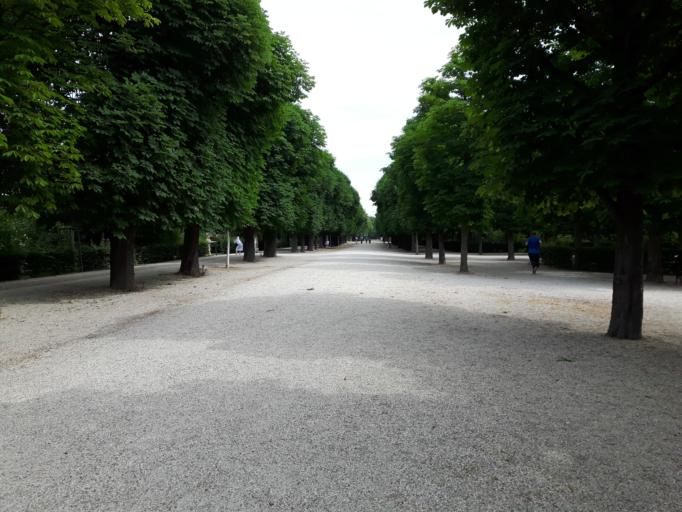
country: AT
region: Vienna
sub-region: Wien Stadt
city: Vienna
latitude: 48.1843
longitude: 16.3040
